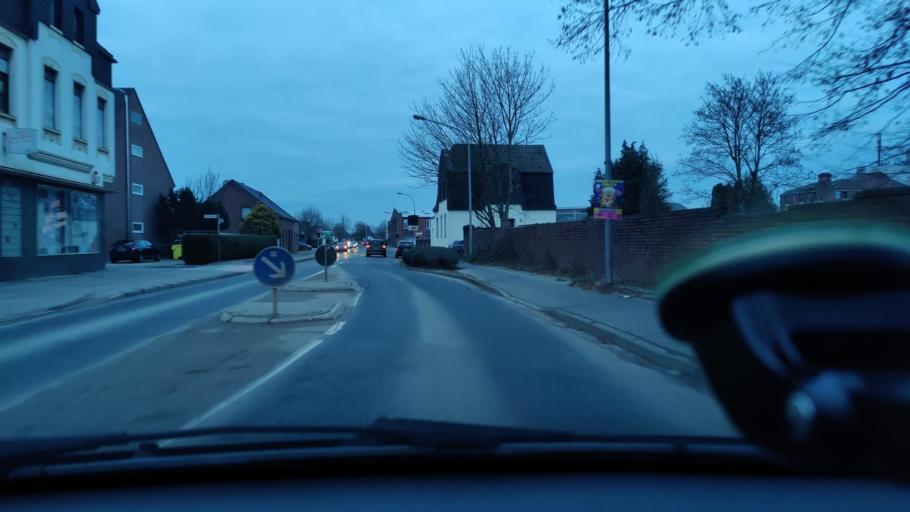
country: DE
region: North Rhine-Westphalia
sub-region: Regierungsbezirk Dusseldorf
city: Viersen
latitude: 51.2930
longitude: 6.3662
